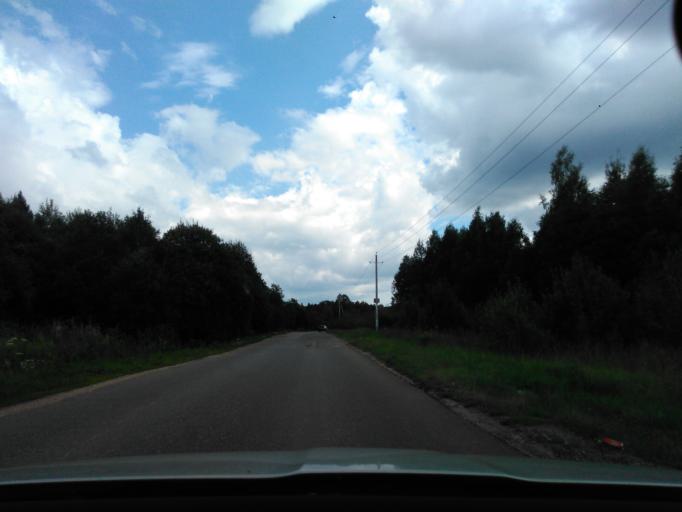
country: RU
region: Moskovskaya
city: Mendeleyevo
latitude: 56.1105
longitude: 37.2366
